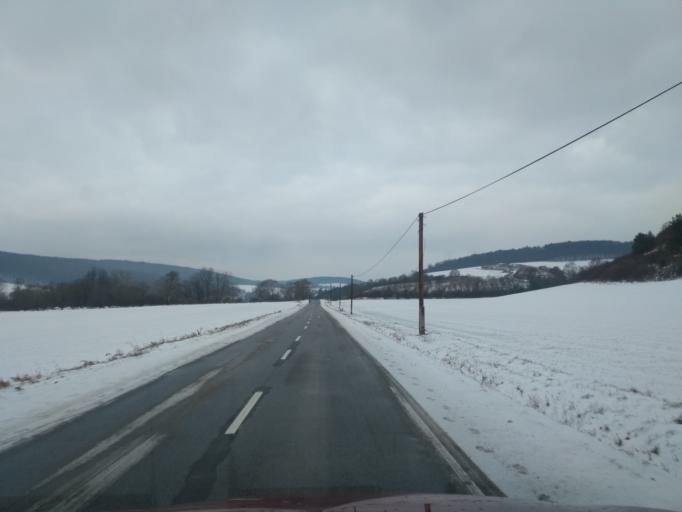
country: SK
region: Presovsky
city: Sabinov
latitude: 49.0191
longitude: 21.1146
